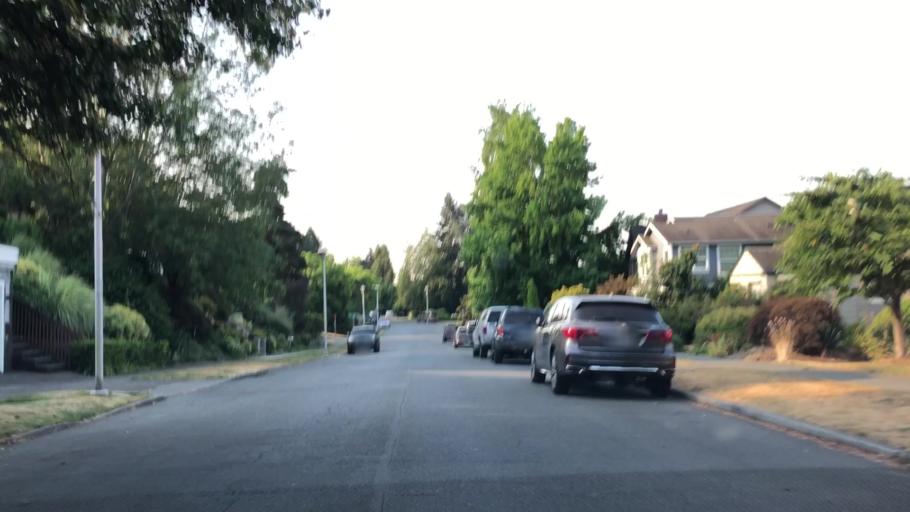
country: US
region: Washington
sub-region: King County
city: Medina
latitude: 47.6570
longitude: -122.2828
